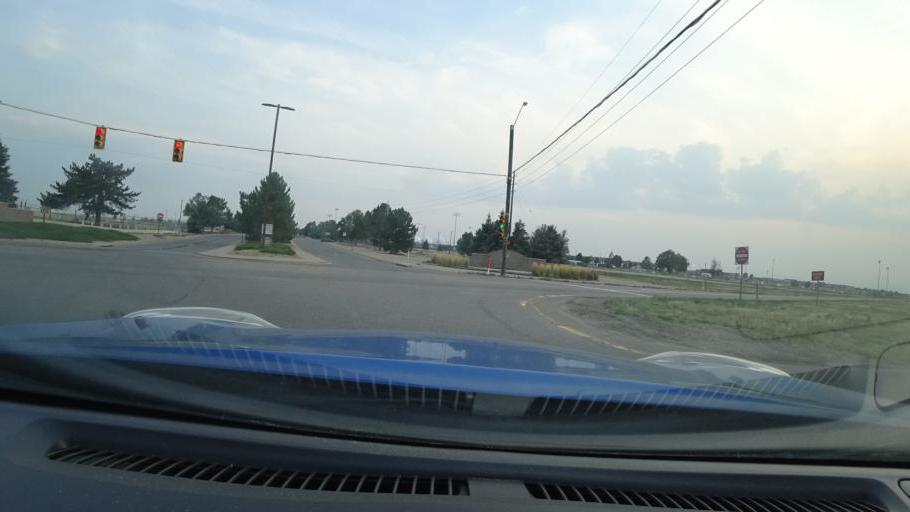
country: US
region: Colorado
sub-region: Adams County
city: Aurora
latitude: 39.7258
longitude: -104.7724
